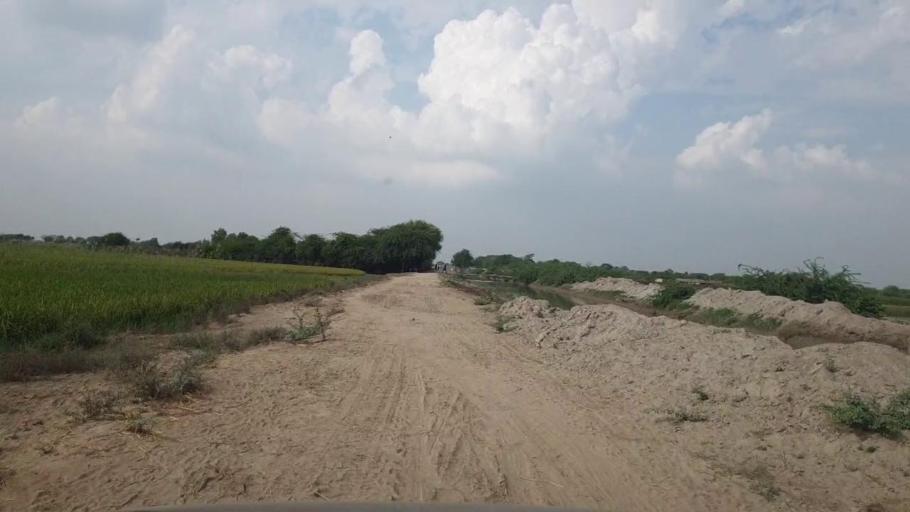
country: PK
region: Sindh
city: Badin
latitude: 24.5642
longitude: 68.6375
